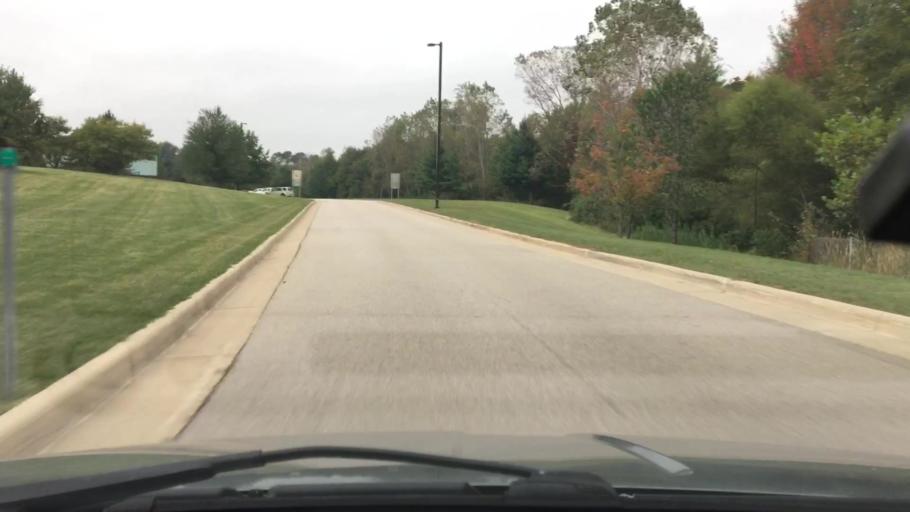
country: US
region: Michigan
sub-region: Berrien County
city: Watervliet
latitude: 42.1816
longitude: -86.2379
